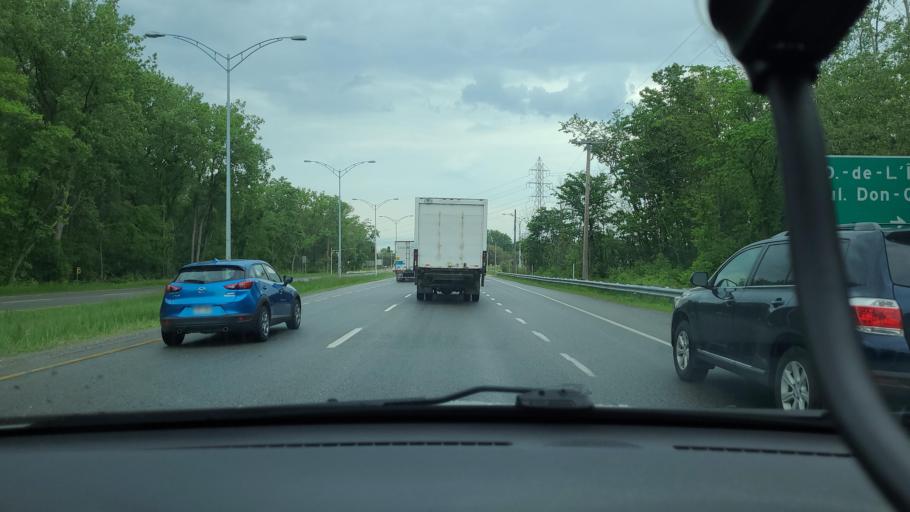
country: CA
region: Quebec
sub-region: Monteregie
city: Pincourt
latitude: 45.3919
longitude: -73.9698
